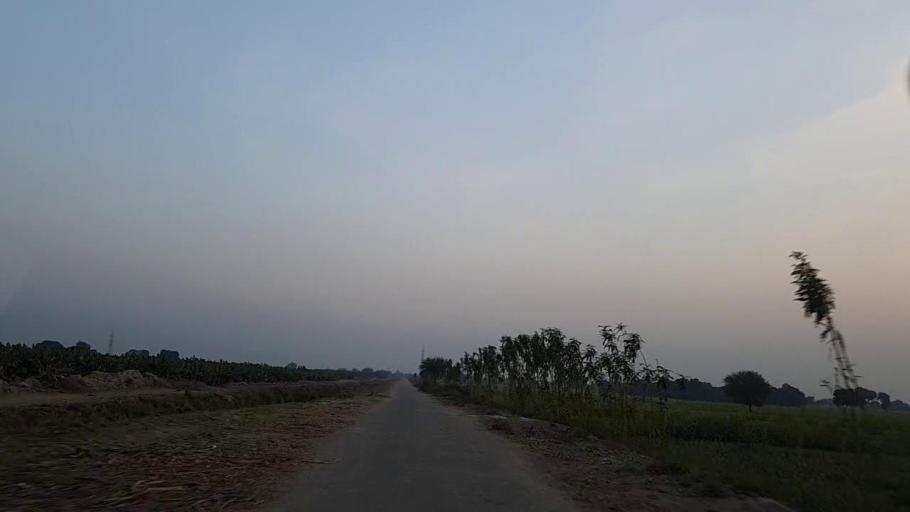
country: PK
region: Sindh
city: Tando Ghulam Ali
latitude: 25.1139
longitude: 68.8989
